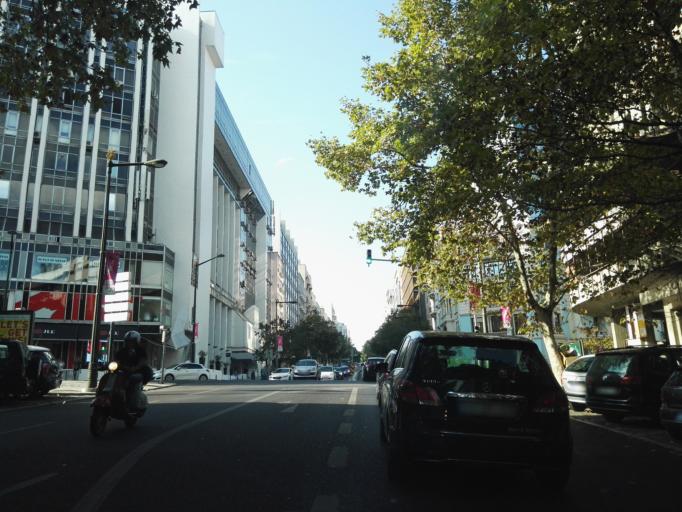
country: PT
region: Lisbon
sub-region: Lisbon
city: Lisbon
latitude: 38.7224
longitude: -9.1511
